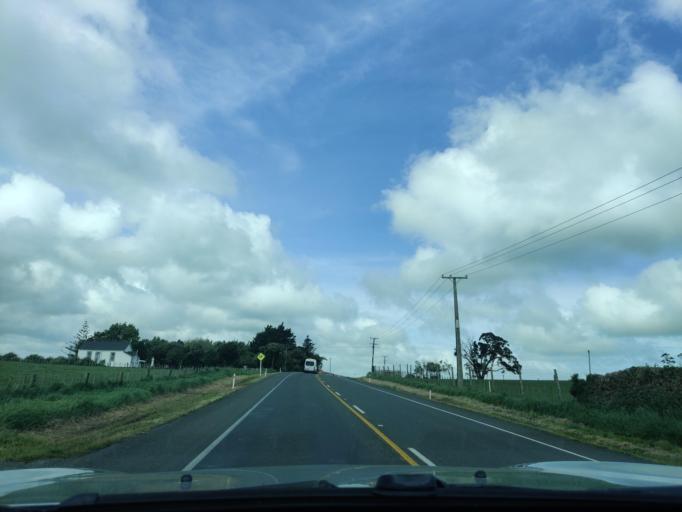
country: NZ
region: Manawatu-Wanganui
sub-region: Wanganui District
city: Wanganui
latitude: -39.8123
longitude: 174.7903
